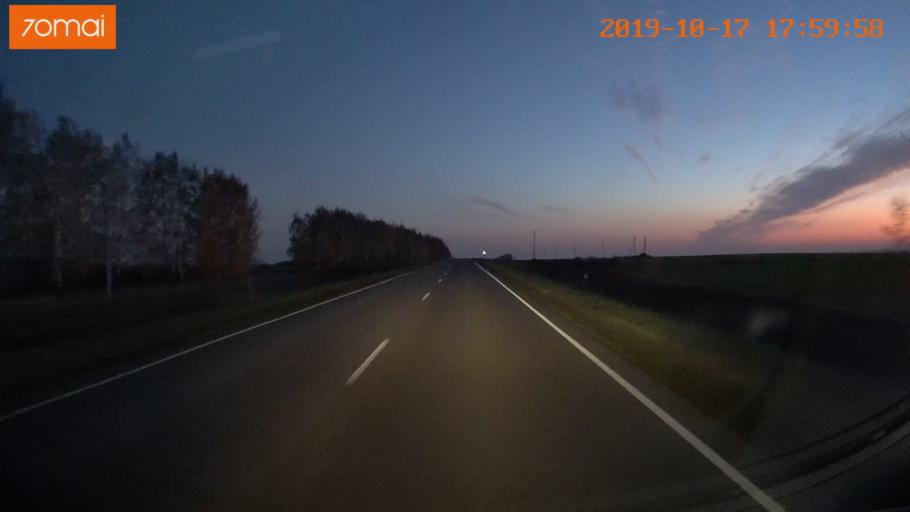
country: RU
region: Tula
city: Kurkino
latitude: 53.5296
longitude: 38.6180
